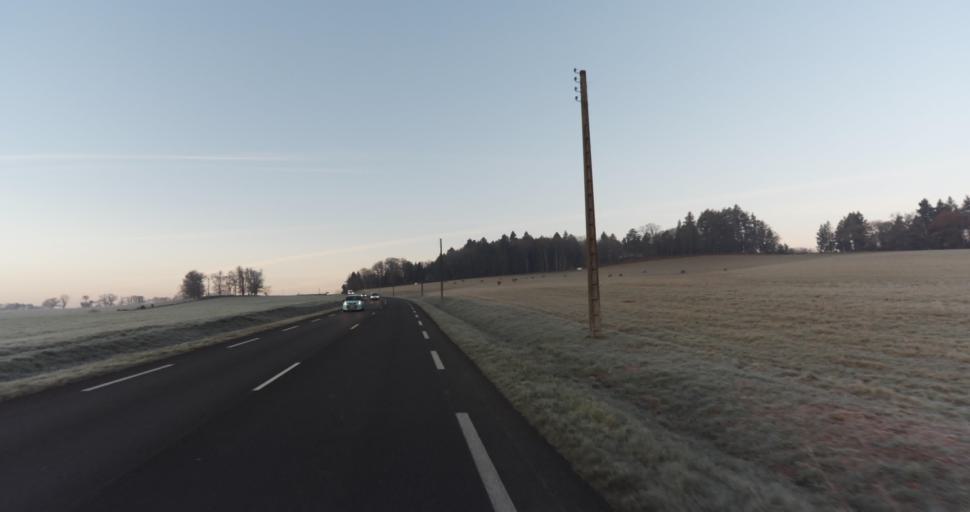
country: FR
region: Limousin
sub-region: Departement de la Haute-Vienne
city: Isle
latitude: 45.8204
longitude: 1.1923
